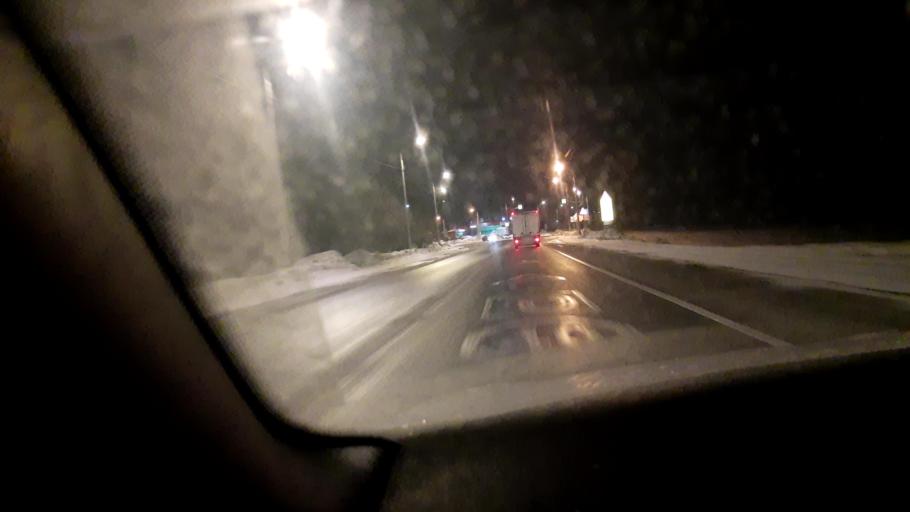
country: RU
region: Moskovskaya
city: Skoropuskovskiy
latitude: 56.3801
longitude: 38.1072
